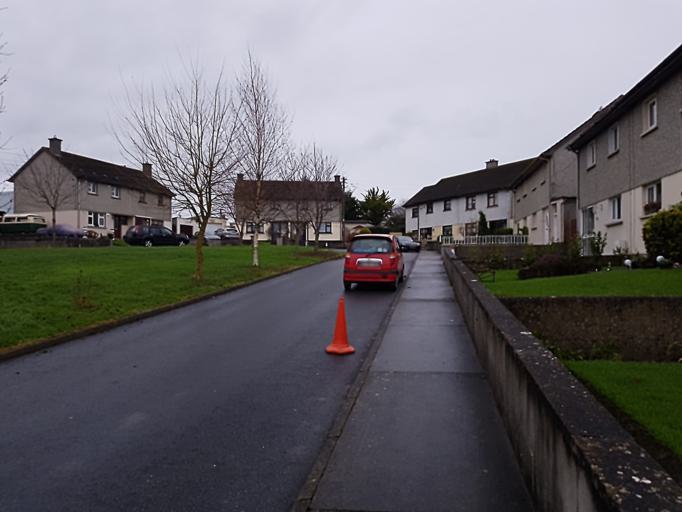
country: IE
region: Leinster
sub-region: Kilkenny
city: Kilkenny
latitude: 52.6566
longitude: -7.2382
